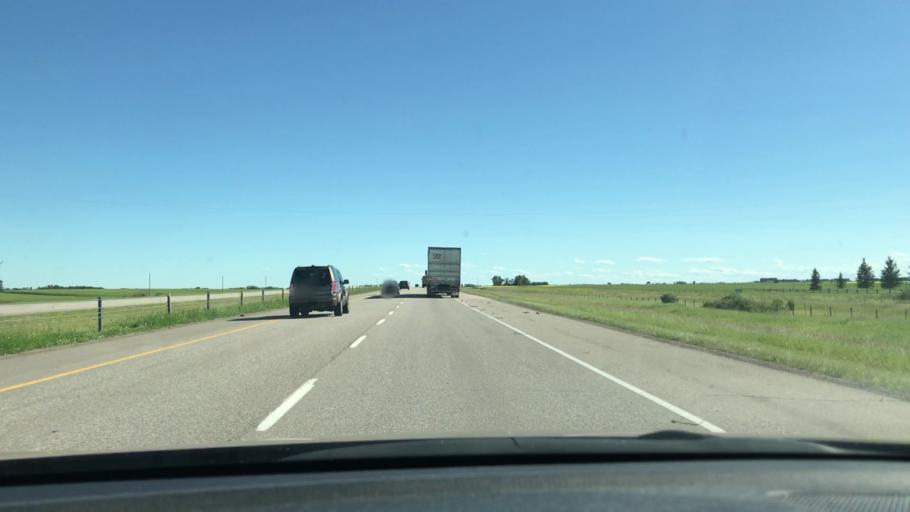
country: CA
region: Alberta
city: Olds
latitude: 51.7223
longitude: -114.0257
